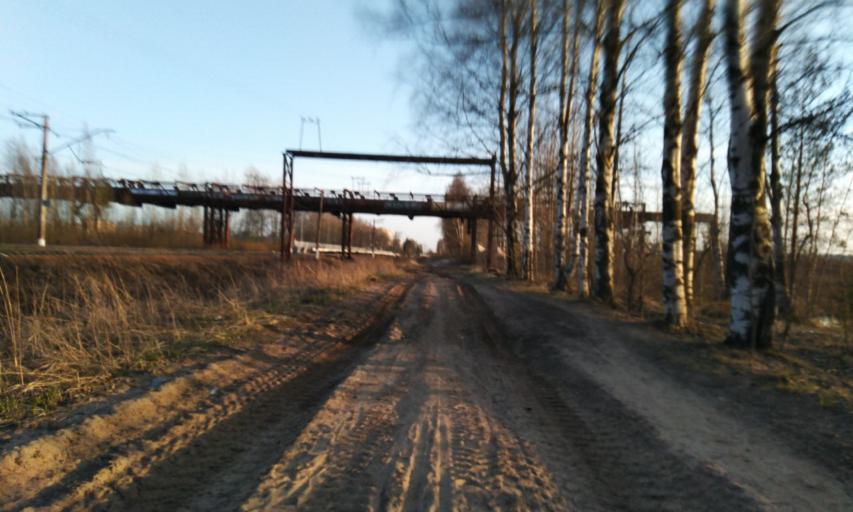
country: RU
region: Leningrad
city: Novoye Devyatkino
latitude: 60.0794
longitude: 30.4616
